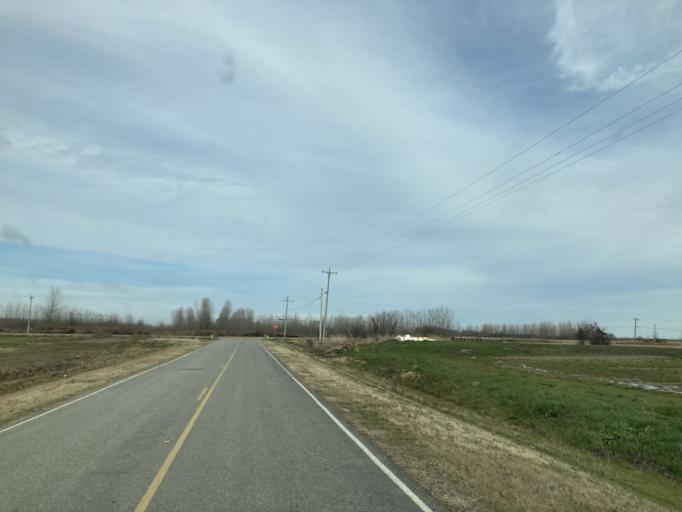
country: US
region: Mississippi
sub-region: Humphreys County
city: Belzoni
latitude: 33.1821
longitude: -90.6065
